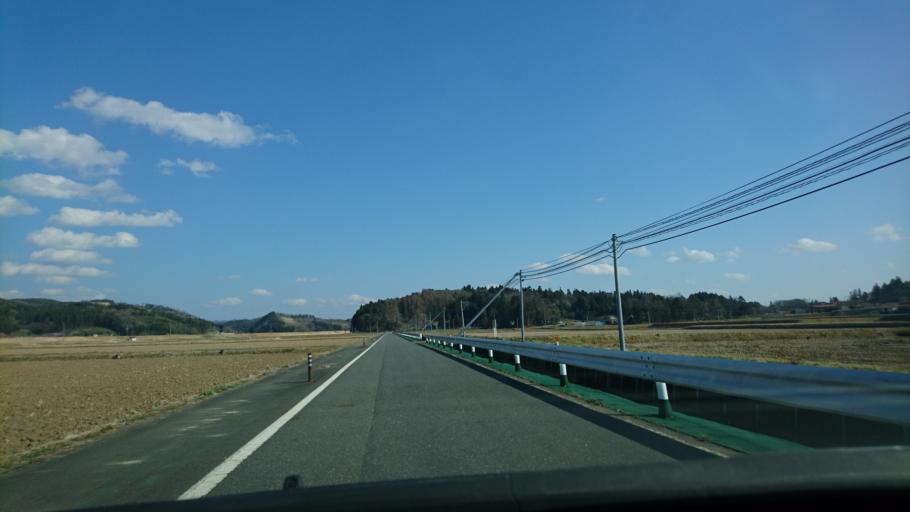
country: JP
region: Iwate
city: Ichinoseki
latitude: 38.8140
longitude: 141.2035
